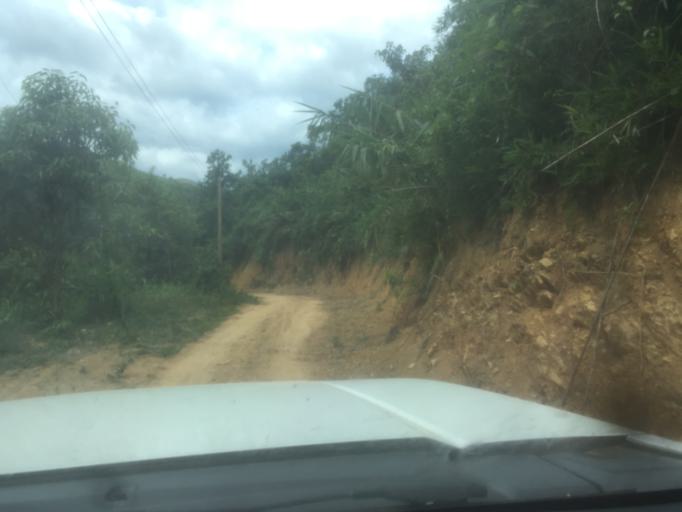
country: LA
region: Phongsali
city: Khoa
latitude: 20.9128
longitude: 102.5601
